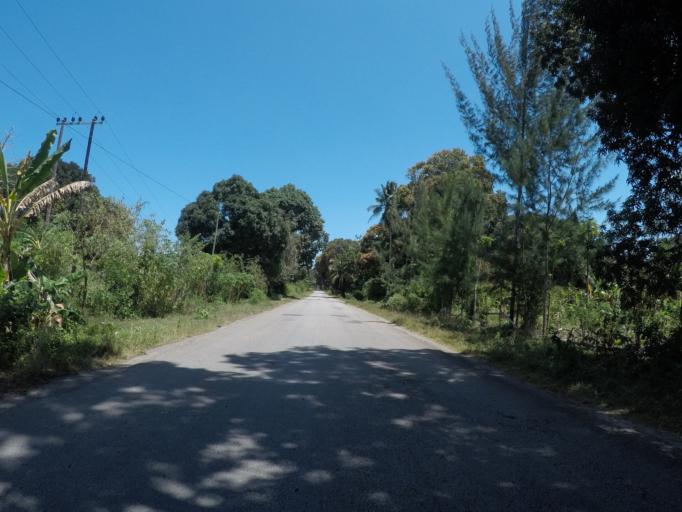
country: TZ
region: Zanzibar Central/South
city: Nganane
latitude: -6.2982
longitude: 39.4349
